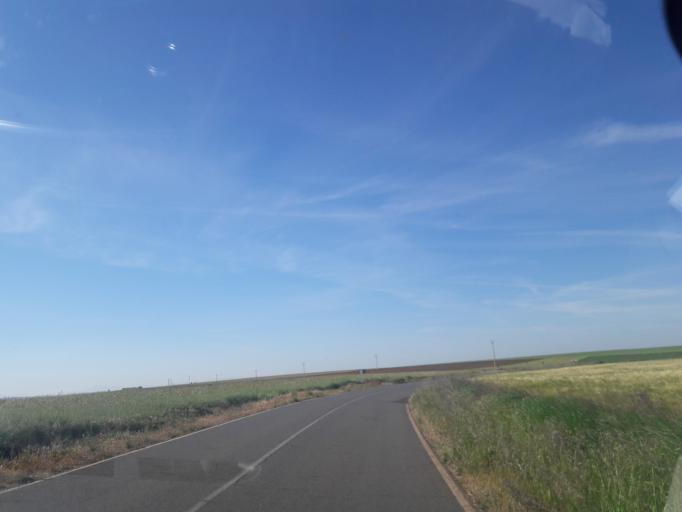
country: ES
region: Castille and Leon
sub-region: Provincia de Salamanca
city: Tardaguila
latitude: 41.1103
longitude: -5.5729
